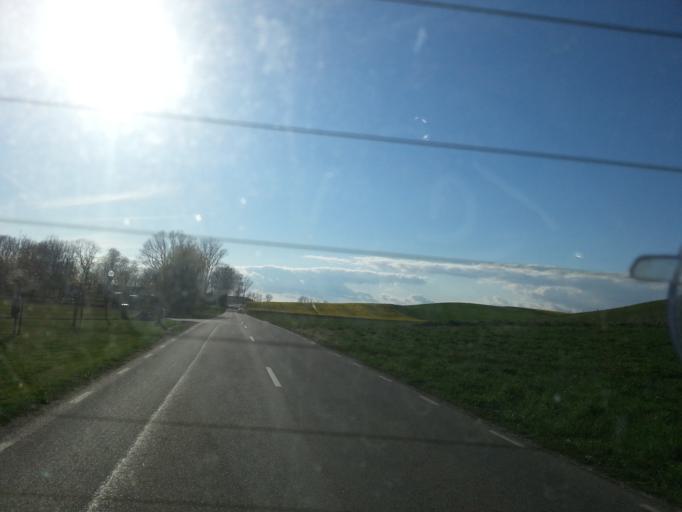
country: SE
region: Skane
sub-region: Ystads Kommun
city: Kopingebro
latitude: 55.3901
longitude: 14.0578
